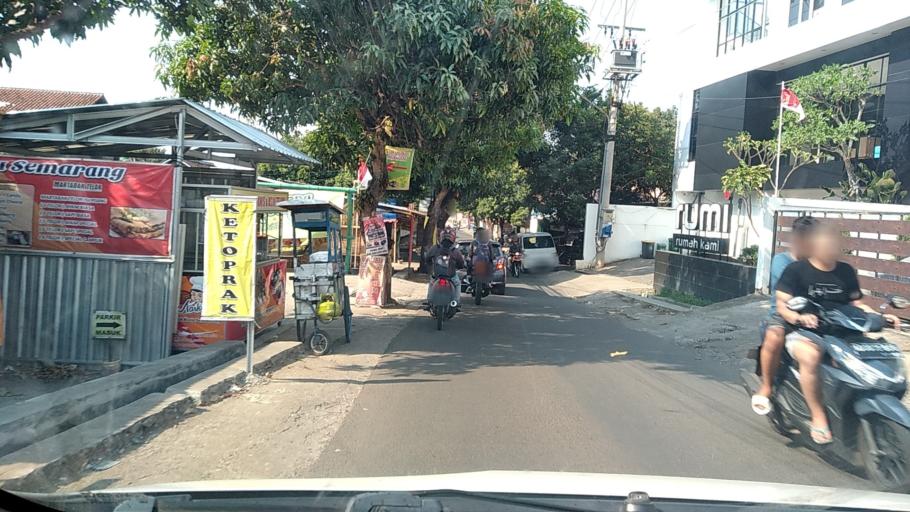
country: ID
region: Central Java
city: Semarang
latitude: -7.0617
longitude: 110.4414
